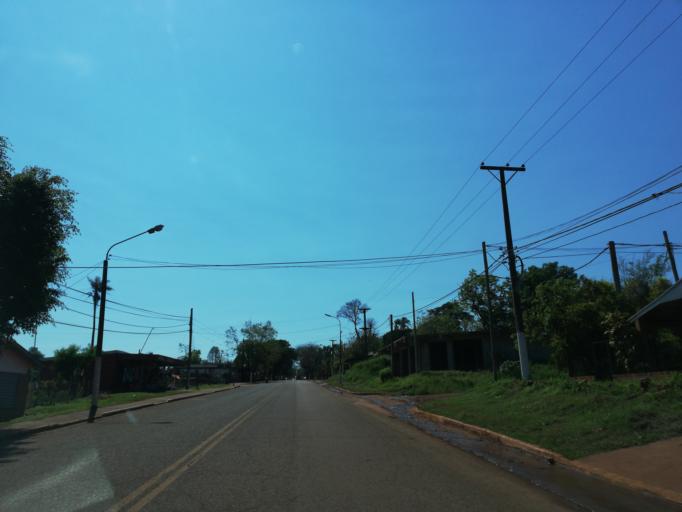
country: AR
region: Misiones
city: Puerto Eldorado
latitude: -26.4100
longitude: -54.6778
